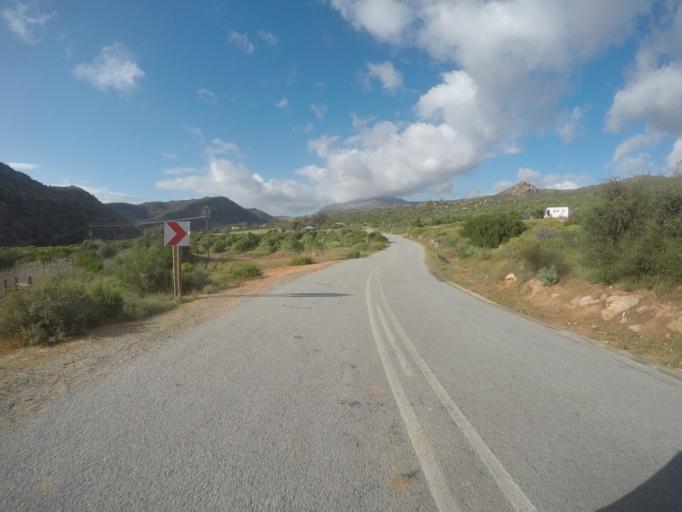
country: ZA
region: Western Cape
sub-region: West Coast District Municipality
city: Clanwilliam
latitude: -32.4329
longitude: 18.9395
